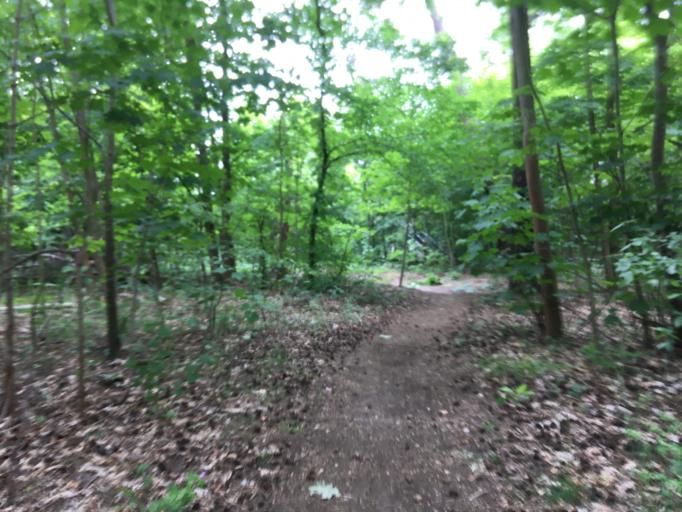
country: DE
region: Berlin
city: Karlshorst
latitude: 52.4701
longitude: 13.5541
